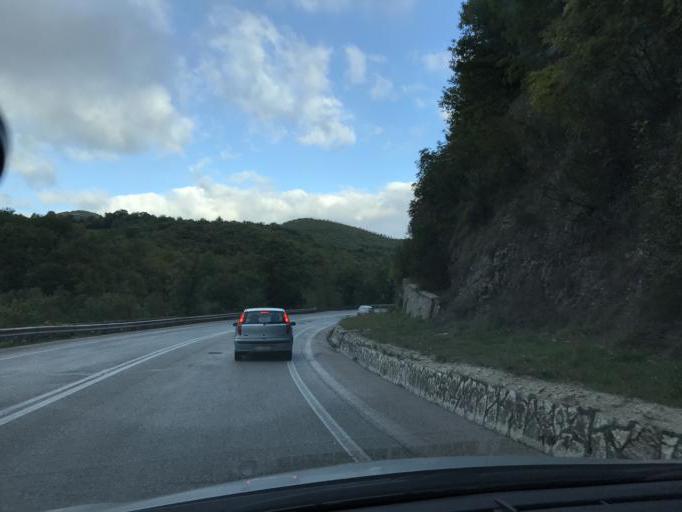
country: IT
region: Umbria
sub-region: Provincia di Terni
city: Ferentillo
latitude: 42.6700
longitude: 12.7295
